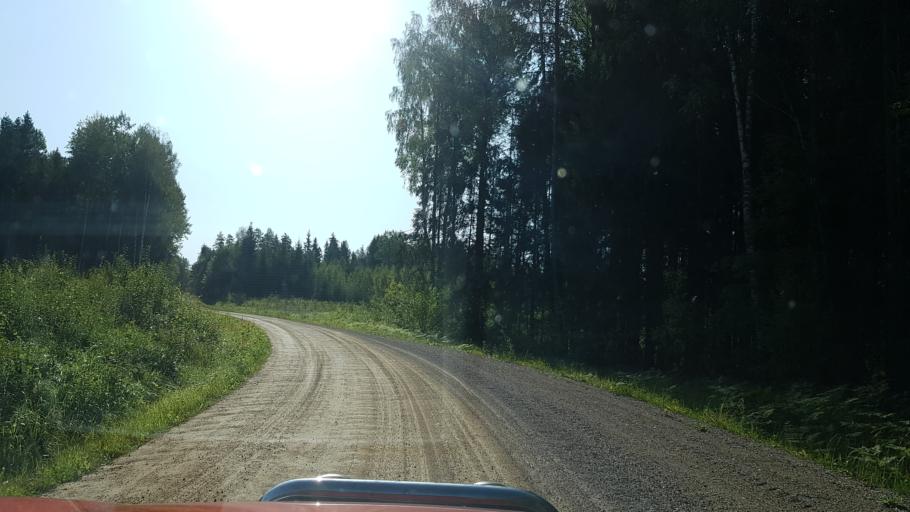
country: LV
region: Apes Novads
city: Ape
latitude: 57.6146
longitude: 26.8187
